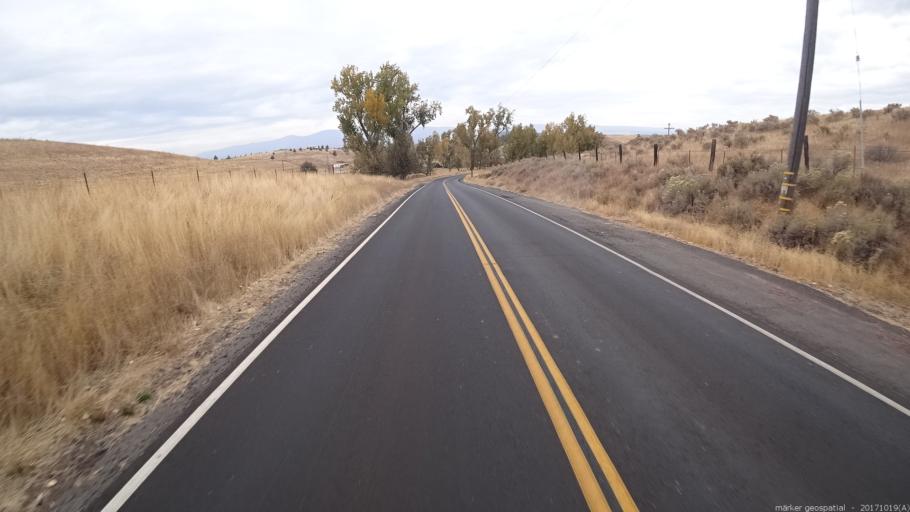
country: US
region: California
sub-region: Shasta County
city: Burney
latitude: 41.0377
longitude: -121.3562
